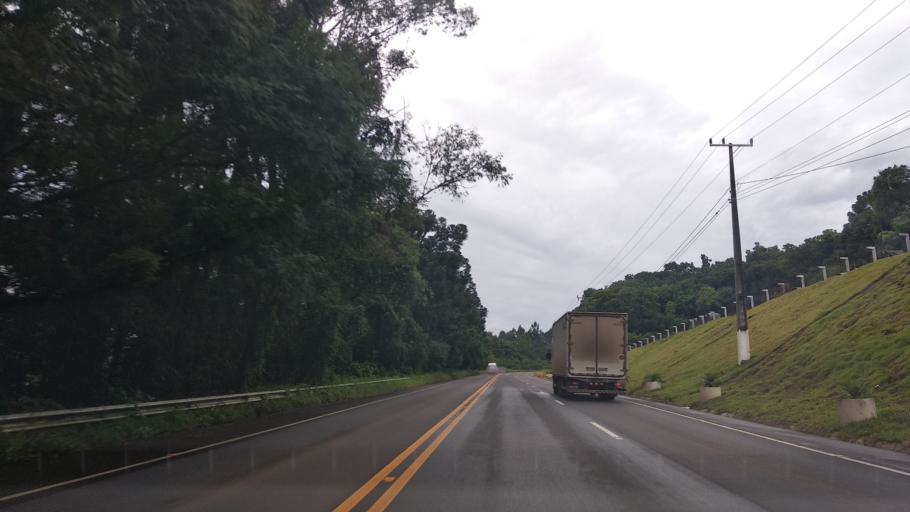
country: BR
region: Santa Catarina
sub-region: Videira
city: Videira
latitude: -27.0699
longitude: -51.2360
